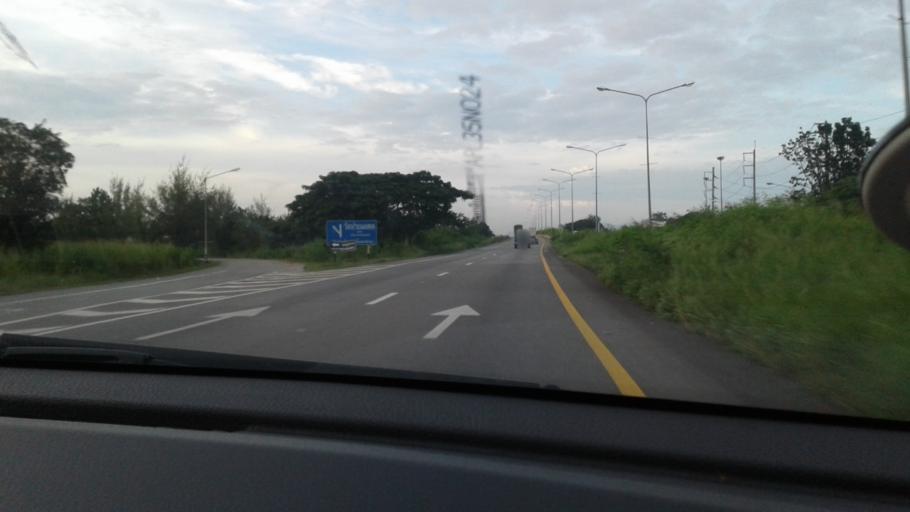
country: TH
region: Prachuap Khiri Khan
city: Hua Hin
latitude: 12.5729
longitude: 99.8674
